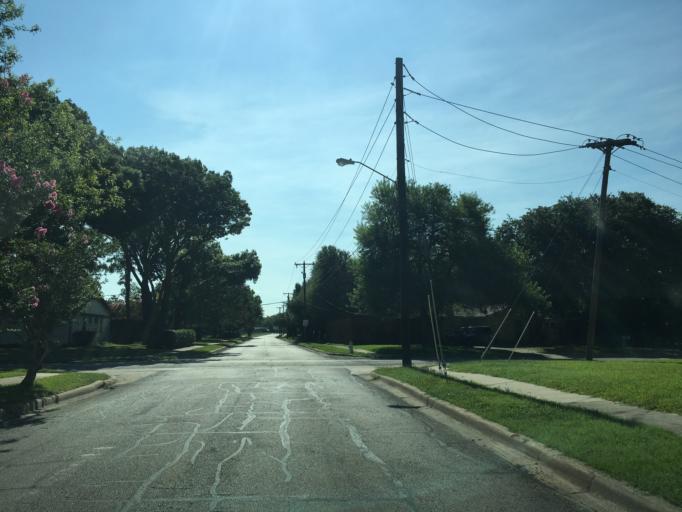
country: US
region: Texas
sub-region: Dallas County
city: Farmers Branch
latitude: 32.9169
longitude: -96.8692
